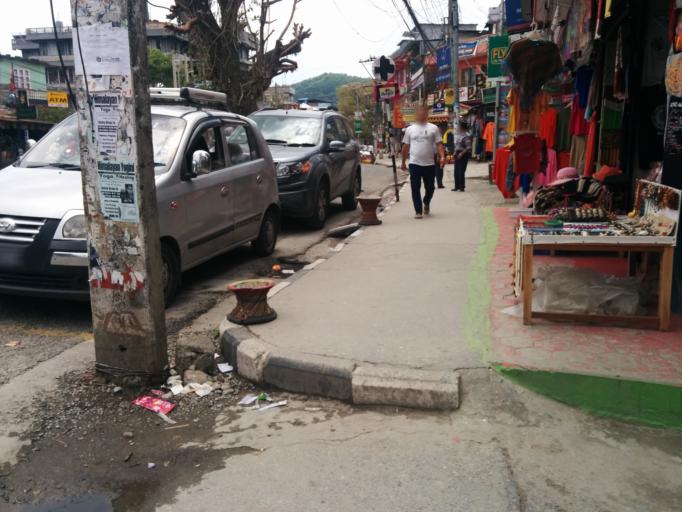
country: NP
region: Western Region
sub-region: Gandaki Zone
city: Pokhara
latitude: 28.2122
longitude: 83.9571
